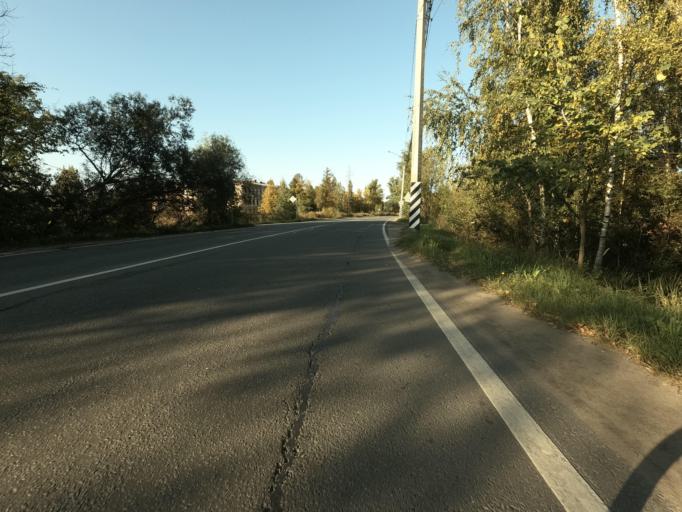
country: RU
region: St.-Petersburg
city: Kolpino
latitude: 59.7548
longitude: 30.6159
